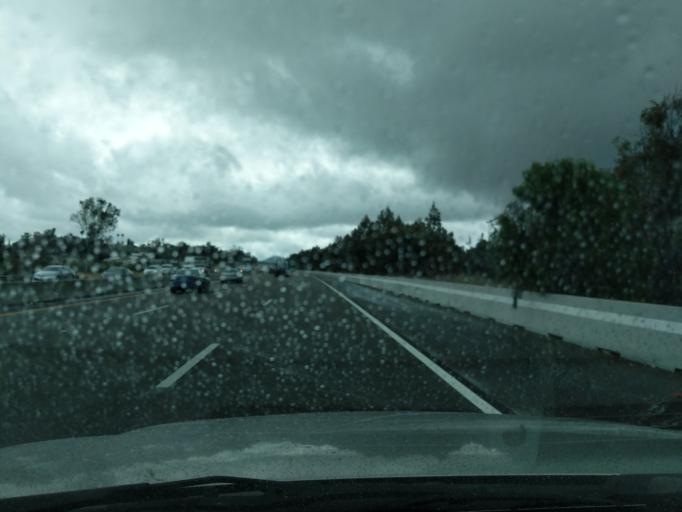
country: US
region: California
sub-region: San Diego County
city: Lake San Marcos
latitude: 33.1570
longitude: -117.2064
